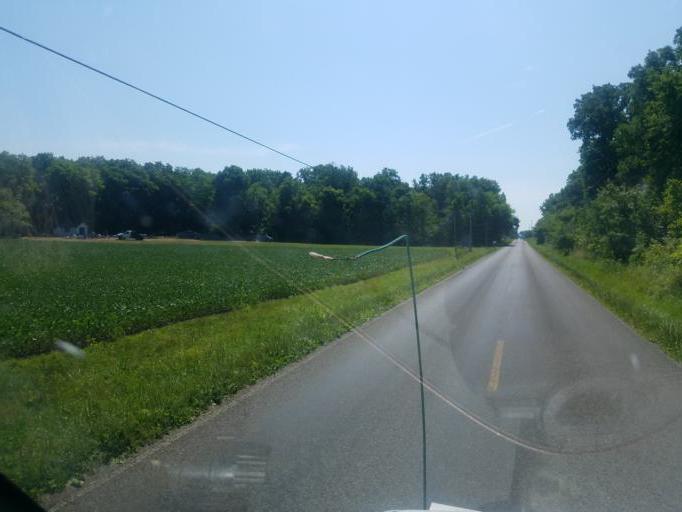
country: US
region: Ohio
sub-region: Champaign County
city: North Lewisburg
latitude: 40.2175
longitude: -83.5114
